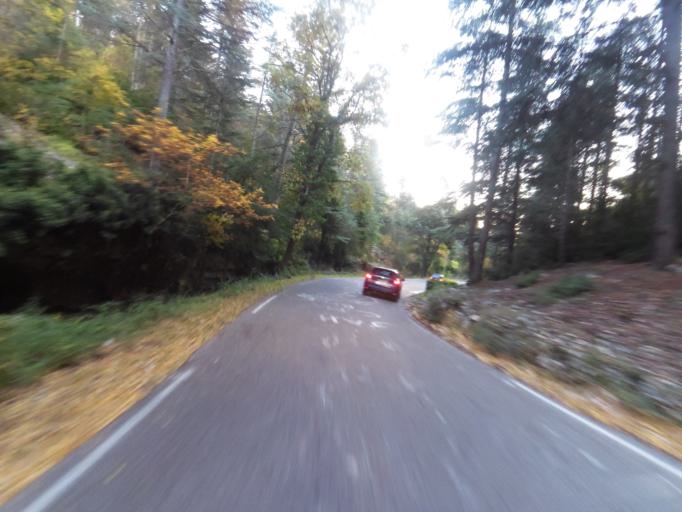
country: FR
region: Provence-Alpes-Cote d'Azur
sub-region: Departement du Vaucluse
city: Villes-sur-Auzon
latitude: 44.1204
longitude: 5.2487
